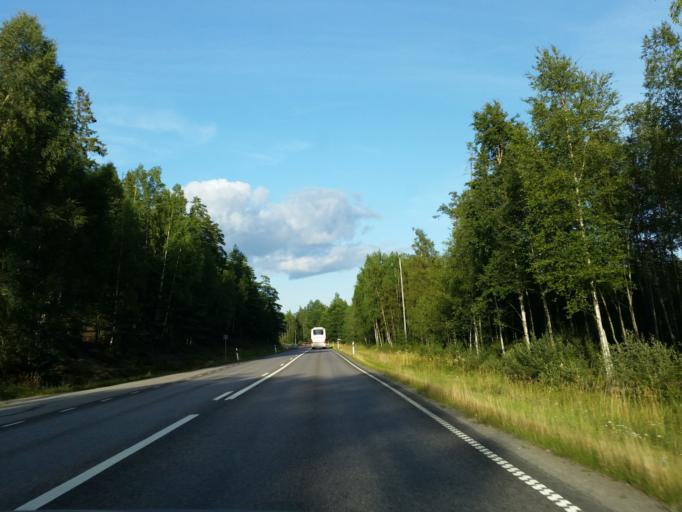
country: SE
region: Stockholm
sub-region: Sodertalje Kommun
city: Molnbo
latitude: 59.0545
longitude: 17.4556
